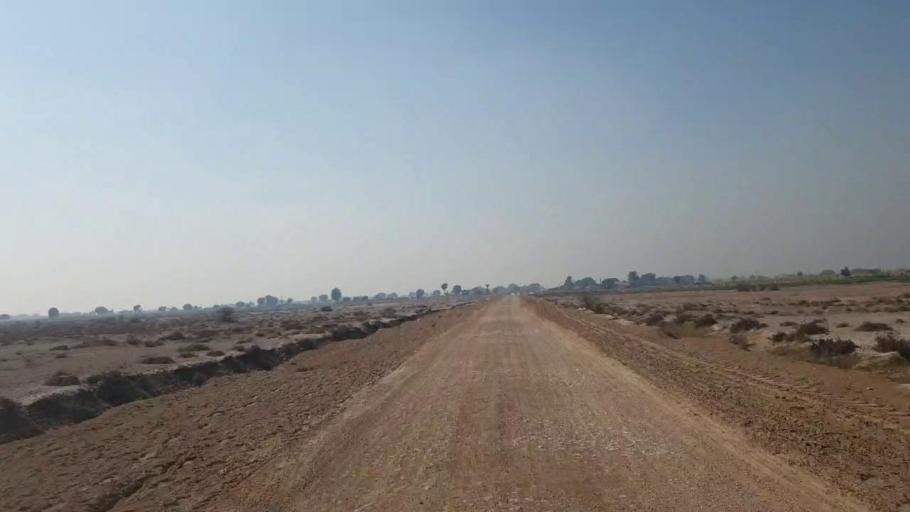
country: PK
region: Sindh
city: Shahpur Chakar
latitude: 26.1125
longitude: 68.6083
